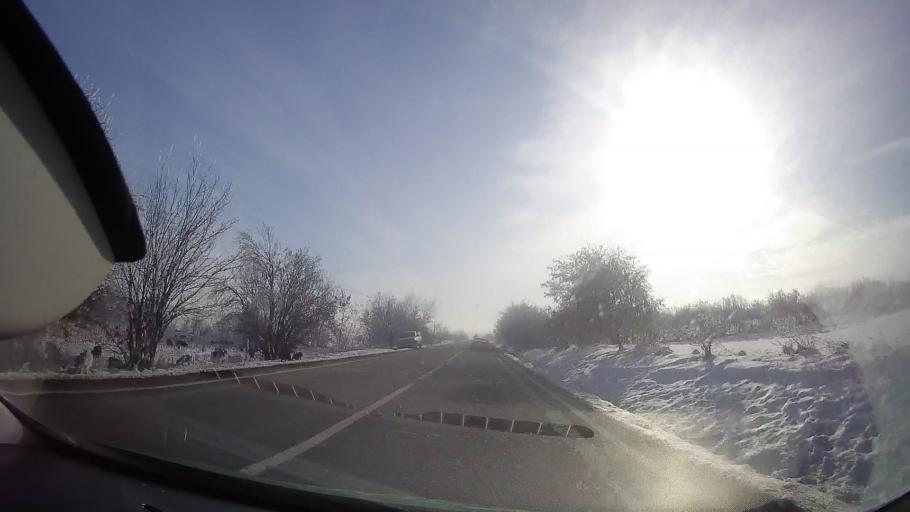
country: RO
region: Neamt
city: Bodesti
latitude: 47.0106
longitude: 26.4243
